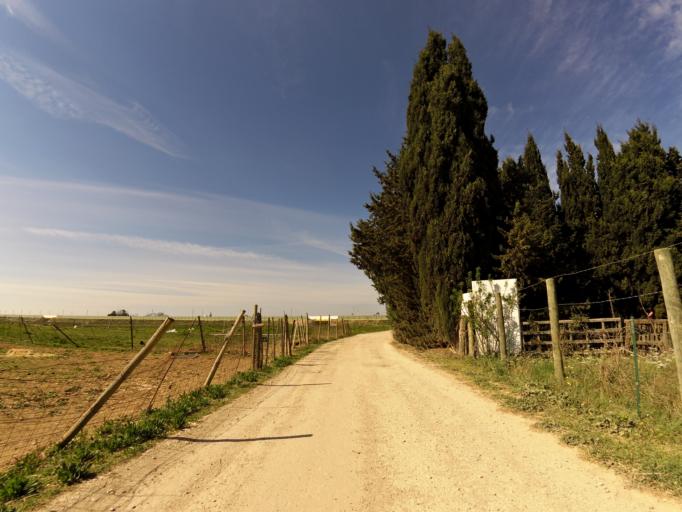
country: FR
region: Languedoc-Roussillon
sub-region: Departement du Gard
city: Aimargues
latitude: 43.7033
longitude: 4.2027
